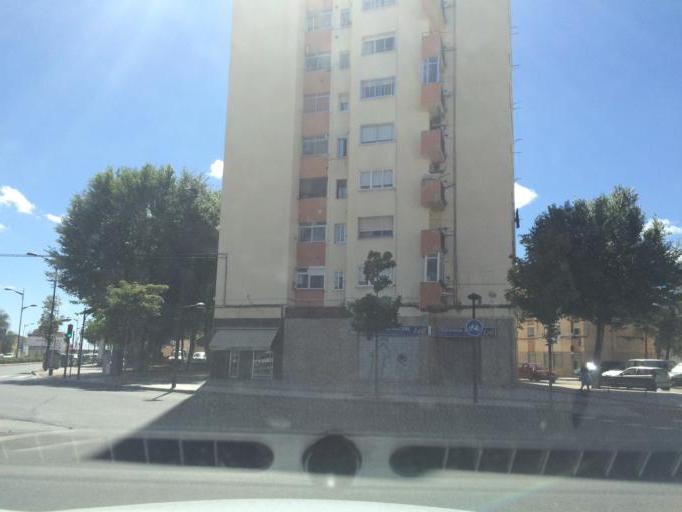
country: ES
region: Castille-La Mancha
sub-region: Provincia de Albacete
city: Albacete
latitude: 38.9843
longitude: -1.8479
